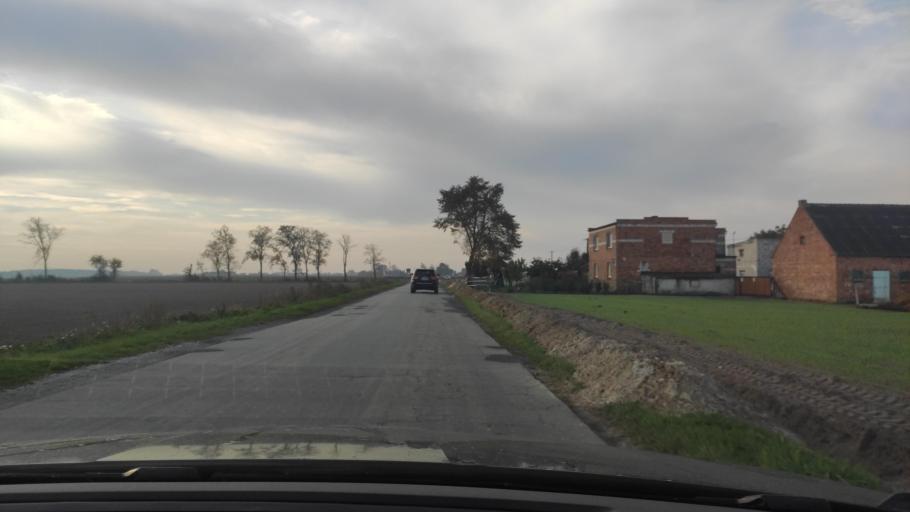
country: PL
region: Greater Poland Voivodeship
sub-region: Powiat poznanski
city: Kleszczewo
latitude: 52.3705
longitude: 17.1671
